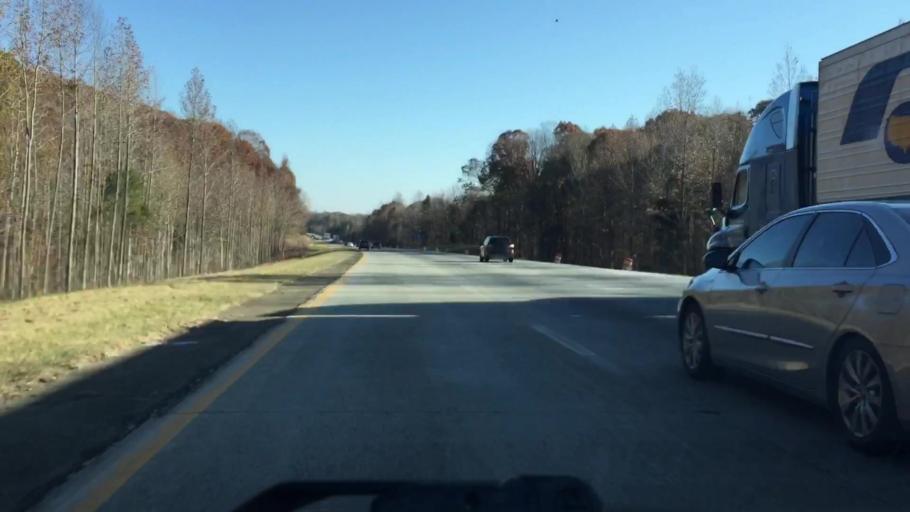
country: US
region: North Carolina
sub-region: Davidson County
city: Thomasville
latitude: 35.8344
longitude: -80.1456
